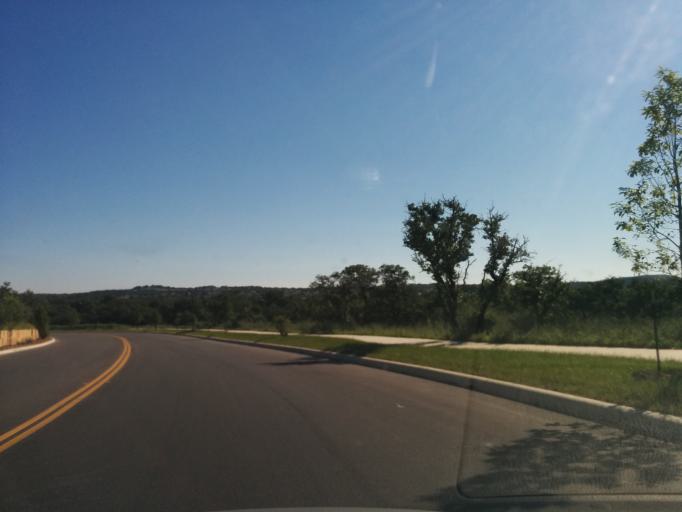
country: US
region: Texas
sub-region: Bexar County
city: Cross Mountain
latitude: 29.6772
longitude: -98.6437
